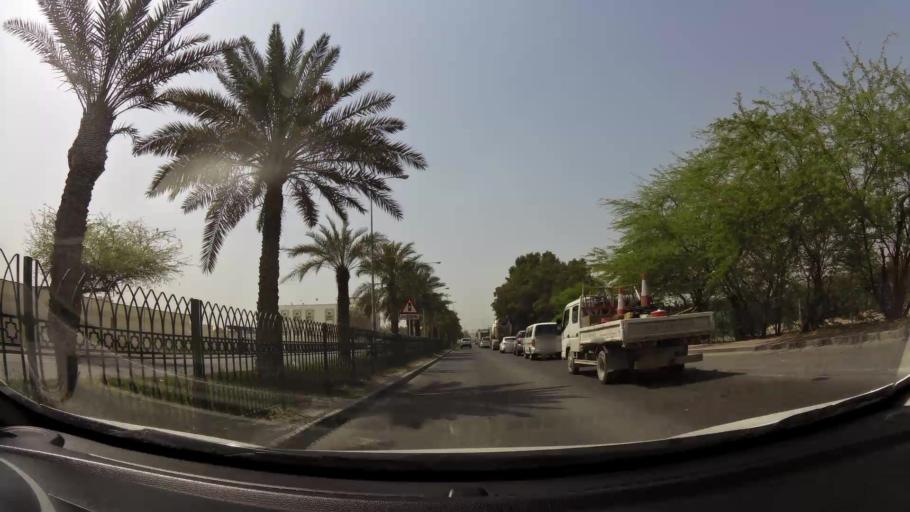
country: BH
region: Manama
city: Jidd Hafs
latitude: 26.2144
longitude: 50.4587
